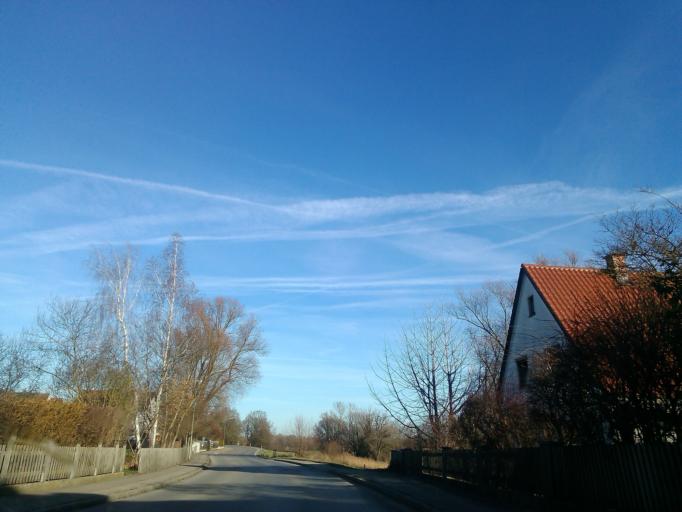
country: DE
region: Bavaria
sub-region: Swabia
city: Aichach
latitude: 48.4725
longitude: 11.1288
